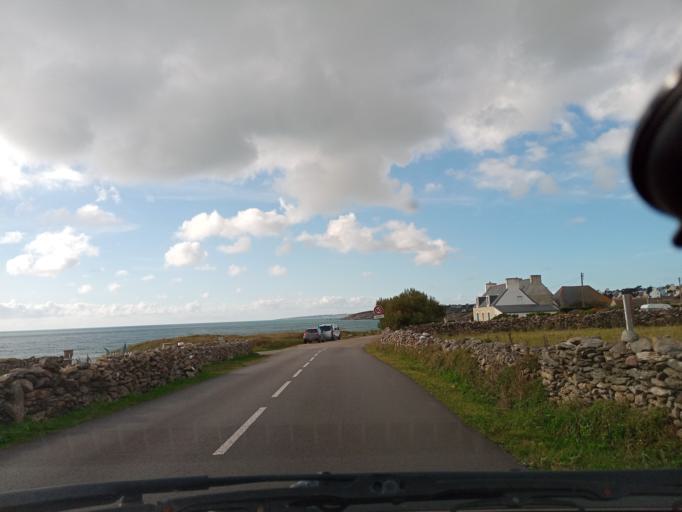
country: FR
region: Brittany
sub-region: Departement du Finistere
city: Plozevet
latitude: 47.9780
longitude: -4.4472
